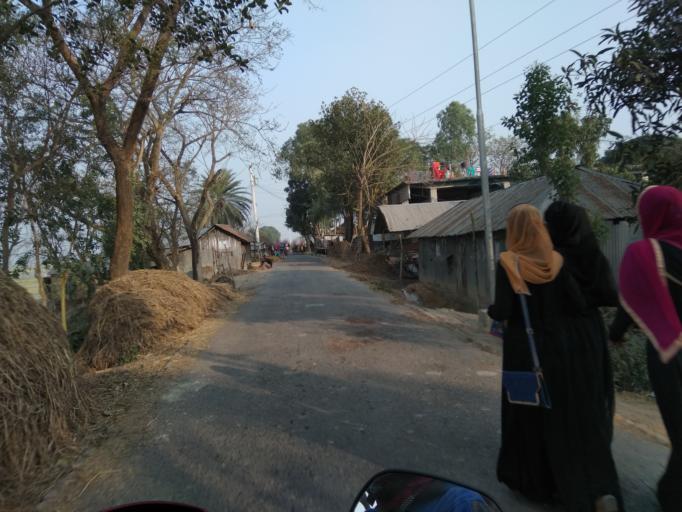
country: BD
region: Rajshahi
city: Par Naogaon
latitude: 24.4989
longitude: 89.1545
